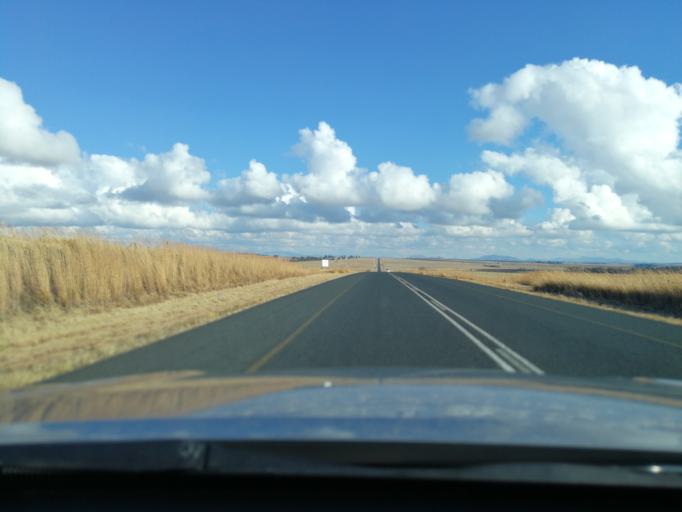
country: ZA
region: Orange Free State
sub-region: Thabo Mofutsanyana District Municipality
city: Bethlehem
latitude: -28.0868
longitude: 28.3555
